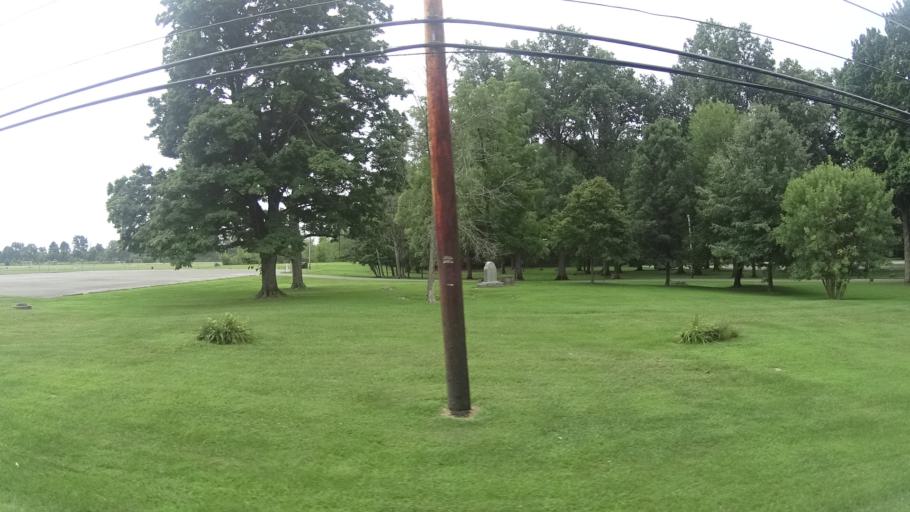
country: US
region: Indiana
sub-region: Madison County
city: Edgewood
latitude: 40.1017
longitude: -85.7464
